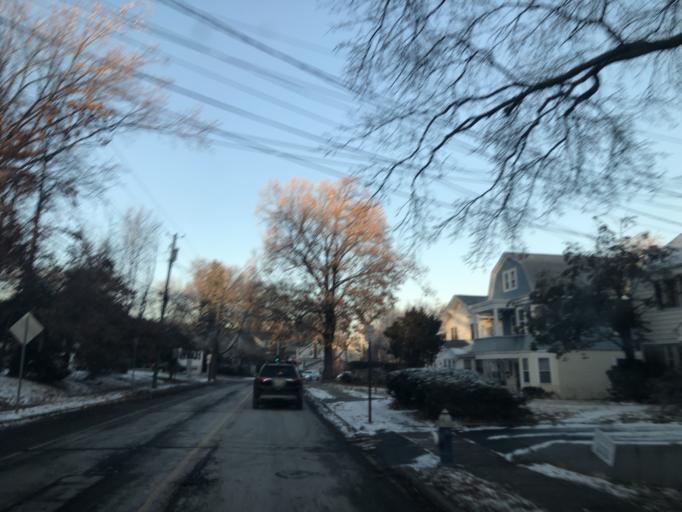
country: US
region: New Jersey
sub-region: Essex County
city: Irvington
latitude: 40.7306
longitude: -74.2512
